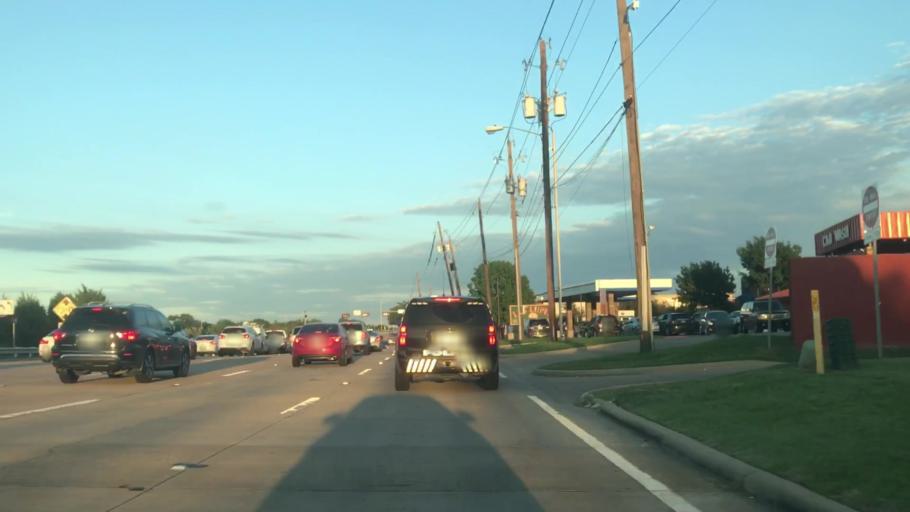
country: US
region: Texas
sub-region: Dallas County
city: Carrollton
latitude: 32.9846
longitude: -96.8918
